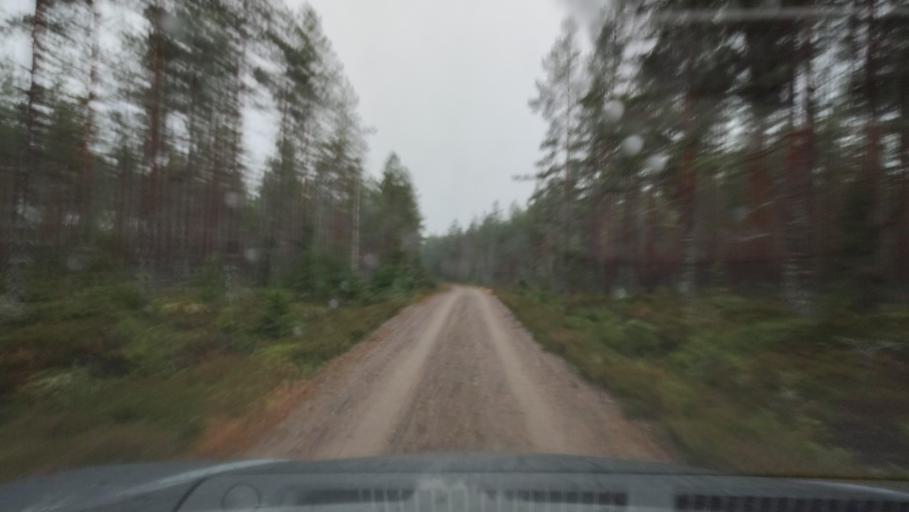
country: FI
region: Southern Ostrobothnia
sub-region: Suupohja
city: Karijoki
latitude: 62.1839
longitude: 21.7345
